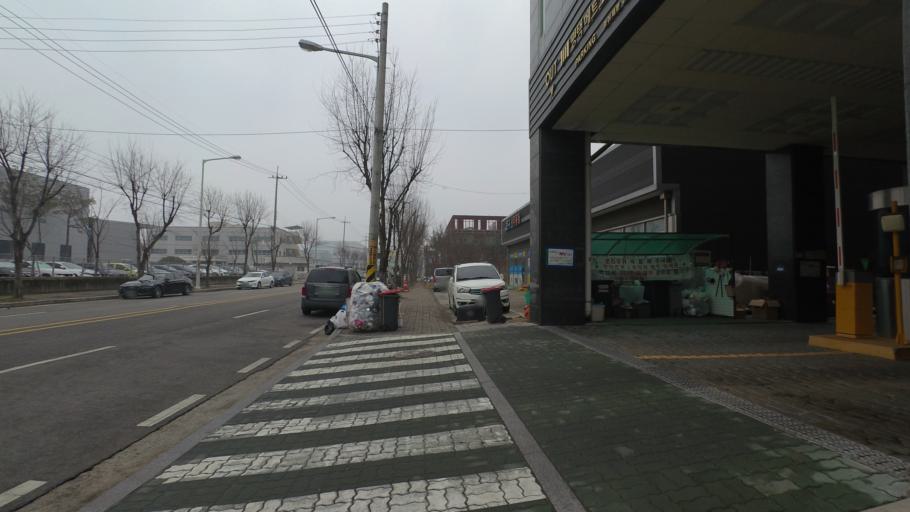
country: KR
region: Chungcheongnam-do
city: Tangjin
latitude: 36.9768
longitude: 126.8442
